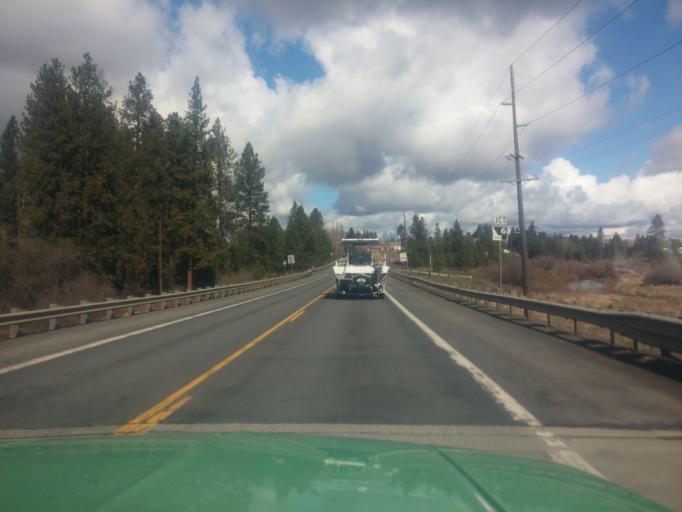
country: US
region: Idaho
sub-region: Latah County
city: Moscow
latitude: 46.9157
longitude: -116.9514
